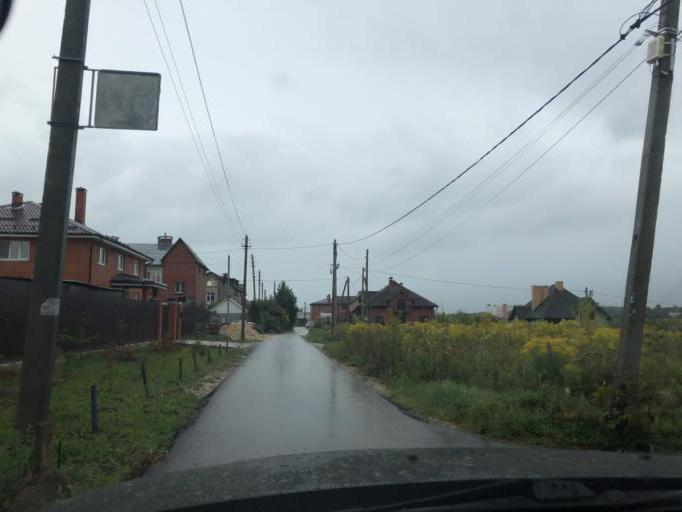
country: RU
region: Tula
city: Barsuki
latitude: 54.1989
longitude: 37.5154
